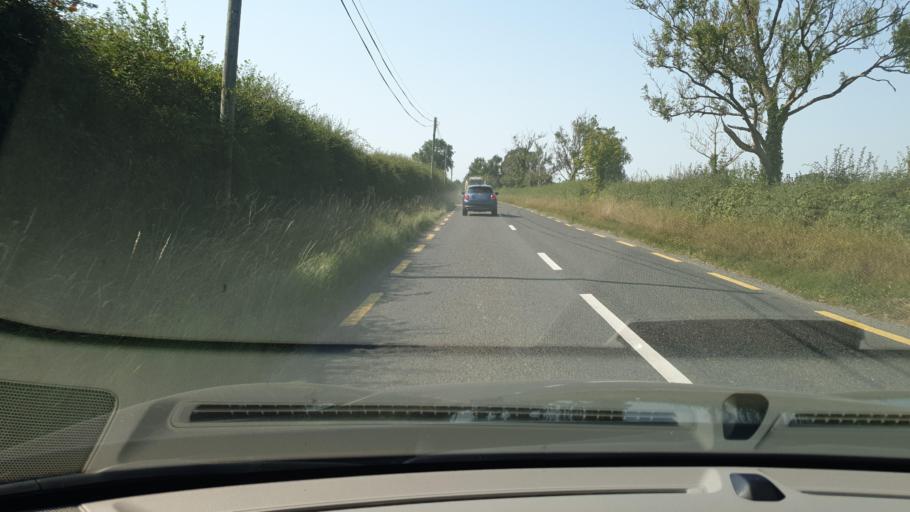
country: IE
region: Leinster
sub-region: An Mhi
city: Trim
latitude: 53.5747
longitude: -6.8304
